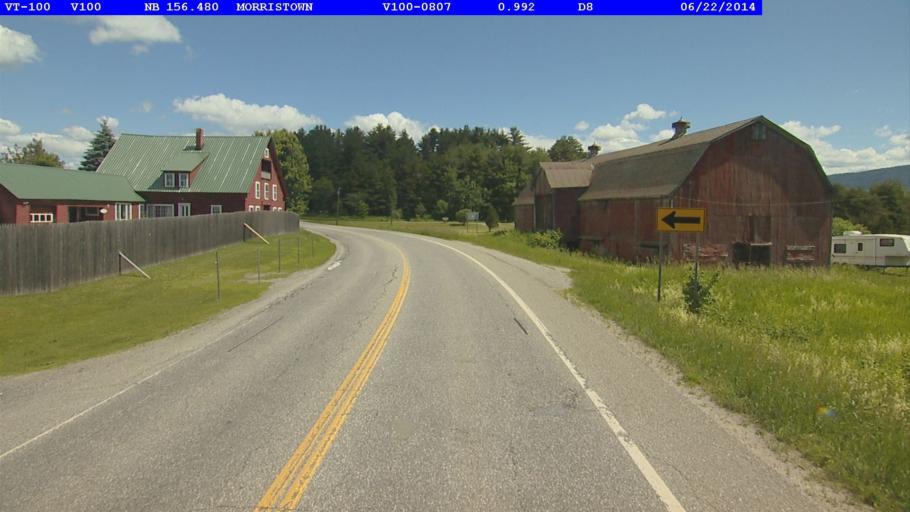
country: US
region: Vermont
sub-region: Lamoille County
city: Morristown
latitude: 44.5072
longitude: -72.6254
